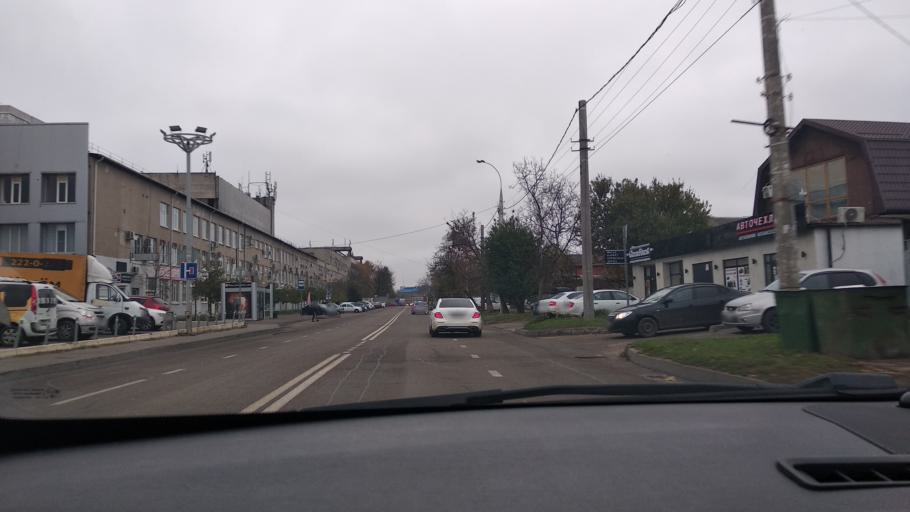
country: RU
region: Krasnodarskiy
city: Krasnodar
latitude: 45.0280
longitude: 39.0215
